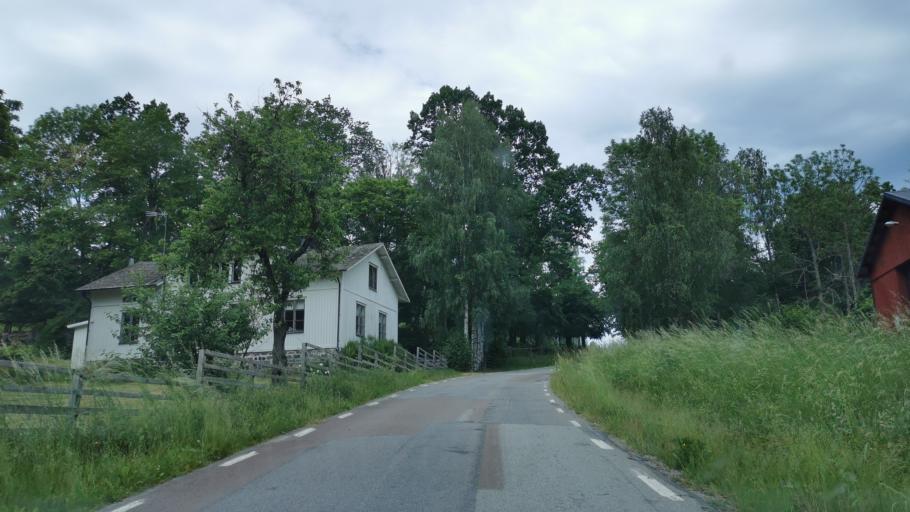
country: SE
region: Vaestra Goetaland
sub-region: Bengtsfors Kommun
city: Dals Langed
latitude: 58.8459
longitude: 12.4077
